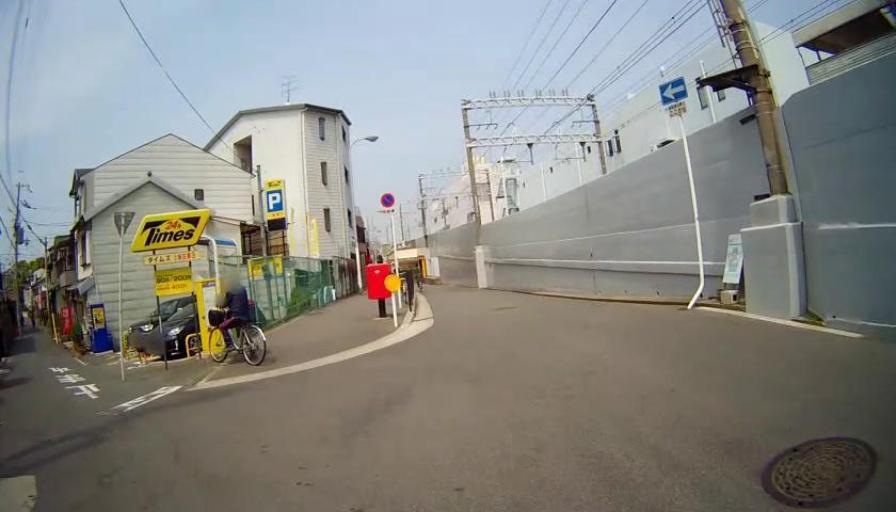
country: JP
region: Osaka
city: Suita
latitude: 34.7476
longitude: 135.5328
